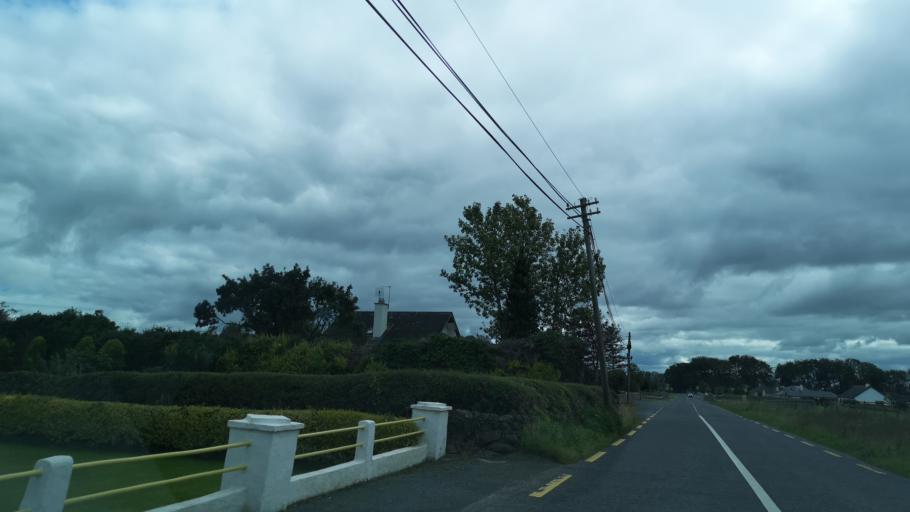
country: IE
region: Connaught
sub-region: County Galway
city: Ballinasloe
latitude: 53.3164
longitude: -8.1702
